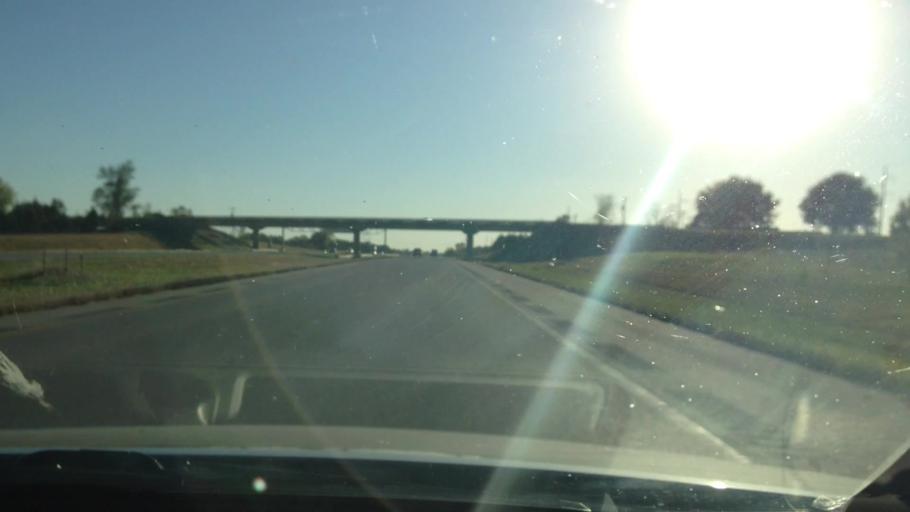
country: US
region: Kansas
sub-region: Johnson County
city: Gardner
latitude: 38.7967
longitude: -94.9073
